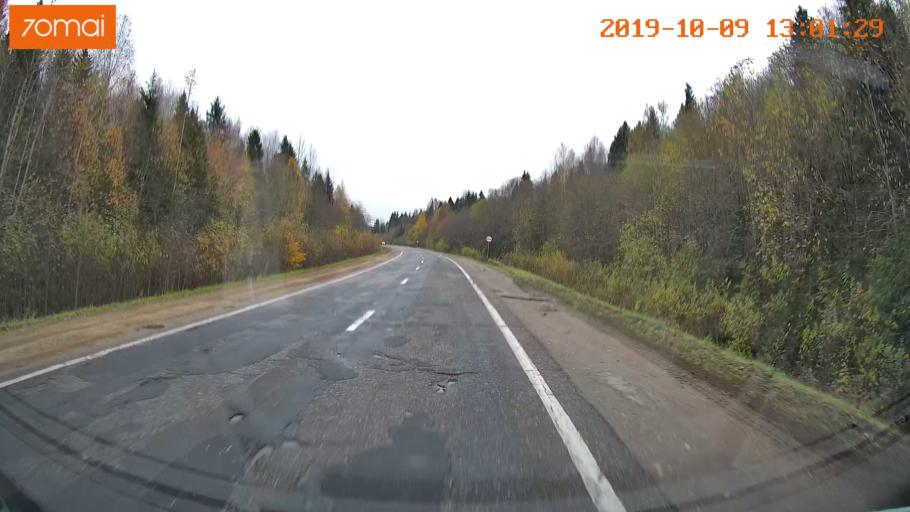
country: RU
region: Jaroslavl
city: Prechistoye
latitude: 58.3679
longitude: 40.4869
